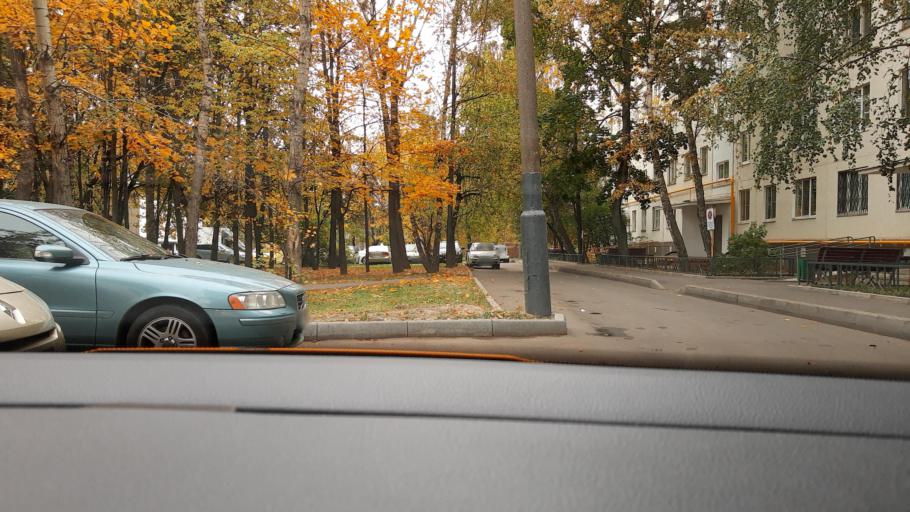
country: RU
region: Moskovskaya
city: Biryulevo Zapadnoye
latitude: 55.5788
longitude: 37.6445
